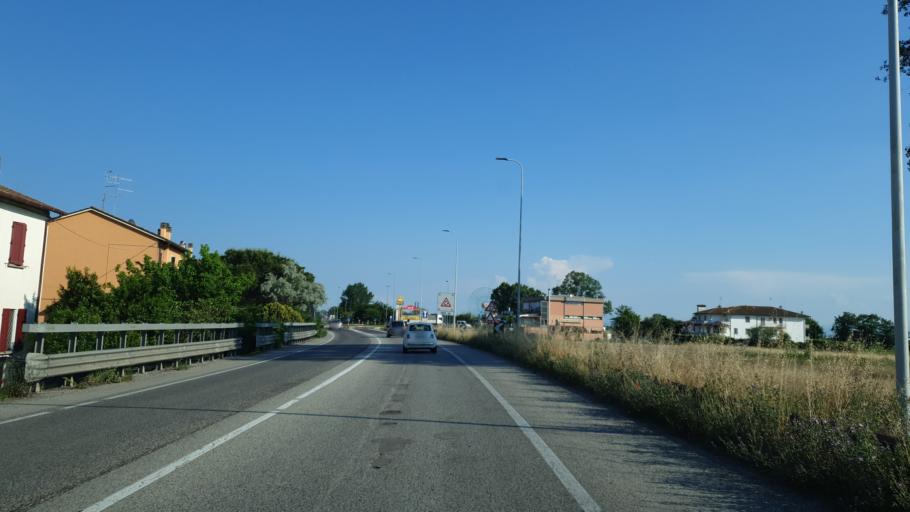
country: IT
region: Emilia-Romagna
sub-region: Provincia di Ravenna
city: Fosso Ghiaia
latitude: 44.3533
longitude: 12.2571
